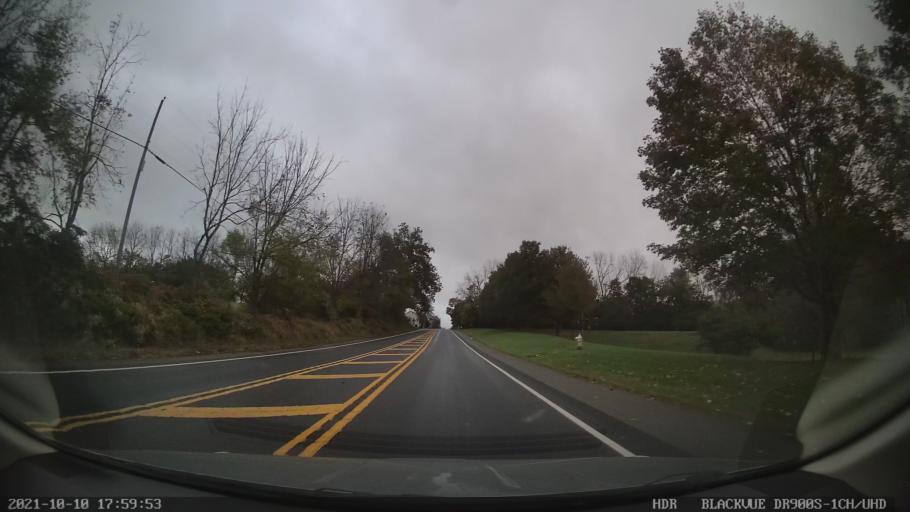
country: US
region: Pennsylvania
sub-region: Lehigh County
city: Egypt
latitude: 40.6415
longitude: -75.5535
